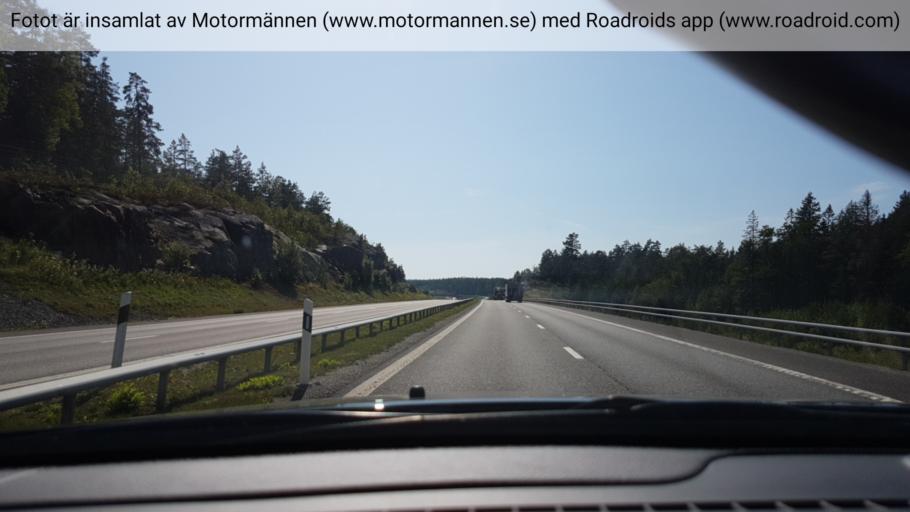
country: SE
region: Stockholm
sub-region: Nynashamns Kommun
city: Osmo
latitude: 59.0328
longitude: 17.9576
